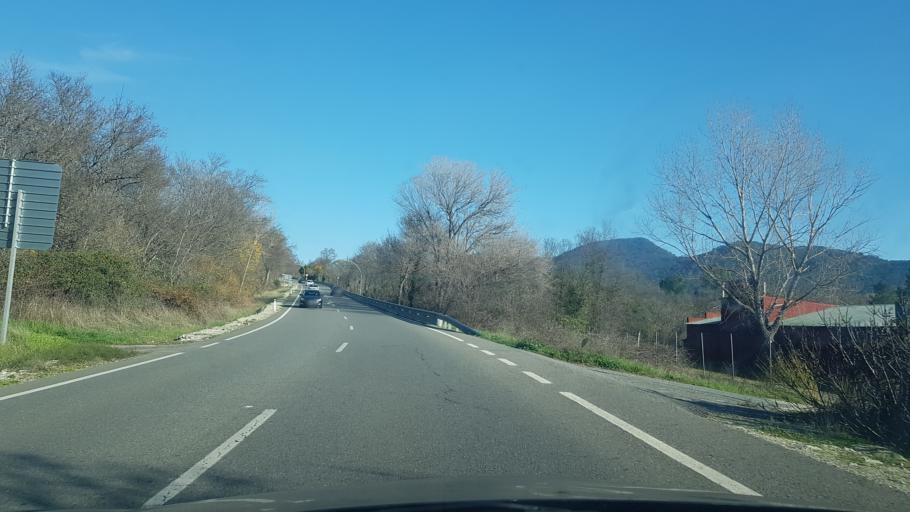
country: ES
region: Castille and Leon
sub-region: Provincia de Avila
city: Sotillo de la Adrada
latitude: 40.3007
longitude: -4.5618
